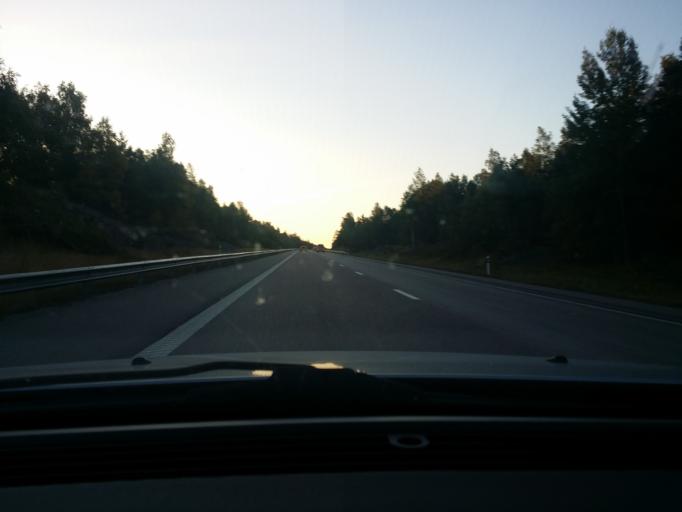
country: SE
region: Uppsala
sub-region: Enkopings Kommun
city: Grillby
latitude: 59.6320
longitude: 17.3114
